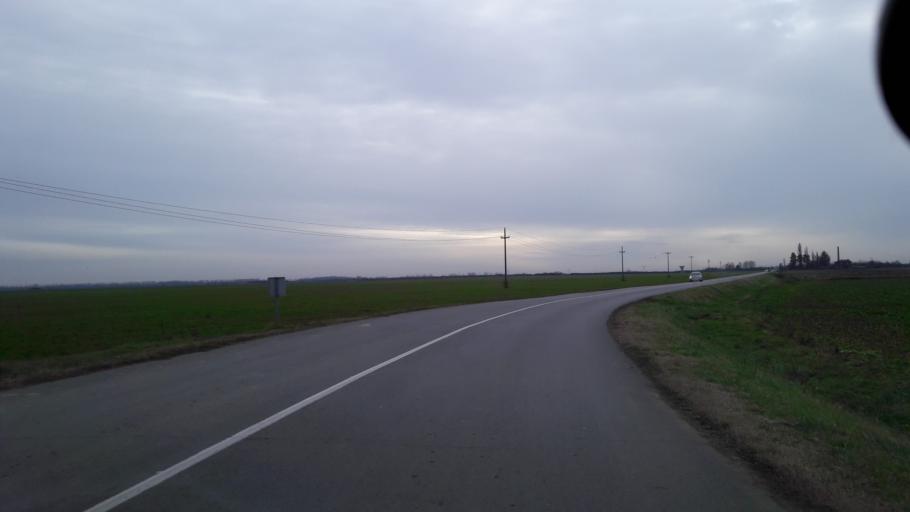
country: HR
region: Osjecko-Baranjska
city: Ovcara
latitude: 45.4890
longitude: 18.5494
